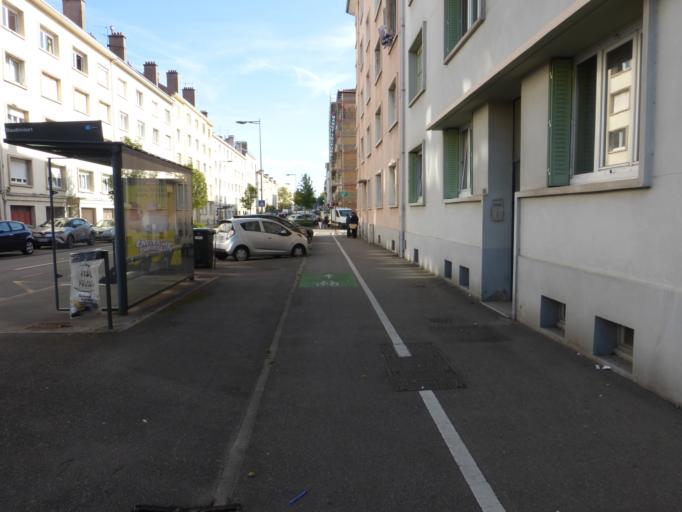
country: FR
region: Lorraine
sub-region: Departement de Meurthe-et-Moselle
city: Villers-les-Nancy
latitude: 48.6777
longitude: 6.1599
